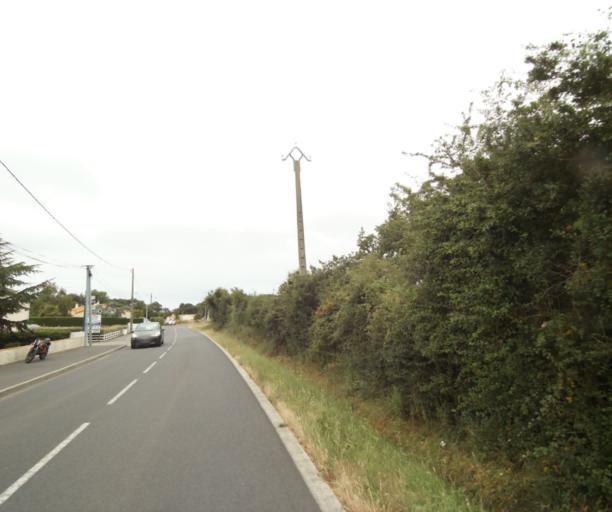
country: FR
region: Pays de la Loire
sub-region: Departement de la Vendee
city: Chateau-d'Olonne
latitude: 46.5107
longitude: -1.7393
